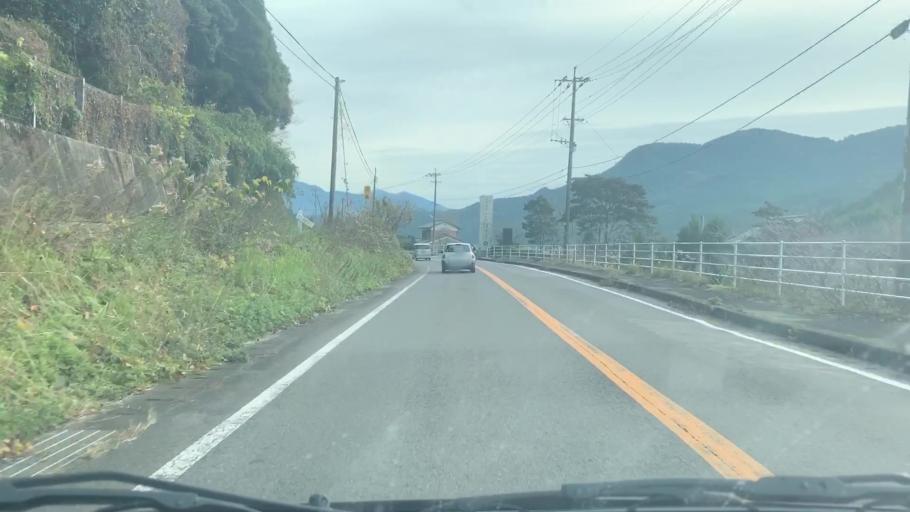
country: JP
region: Saga Prefecture
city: Karatsu
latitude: 33.3368
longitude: 129.9760
